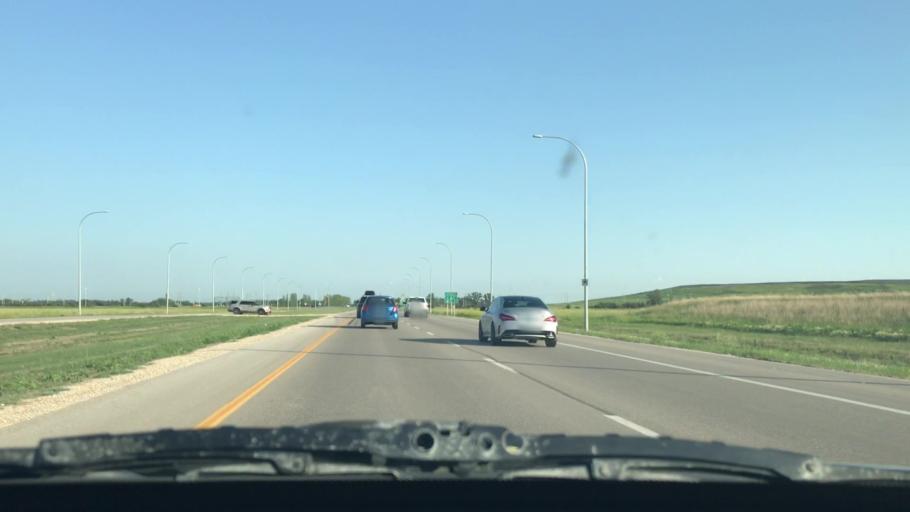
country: CA
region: Manitoba
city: Winnipeg
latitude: 49.7734
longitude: -97.1856
